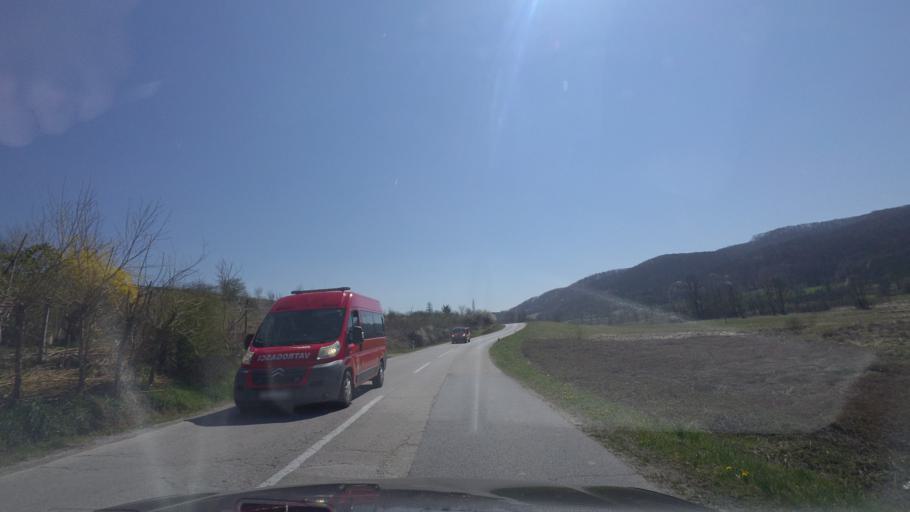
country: HR
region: Karlovacka
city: Vojnic
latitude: 45.3648
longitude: 15.6651
